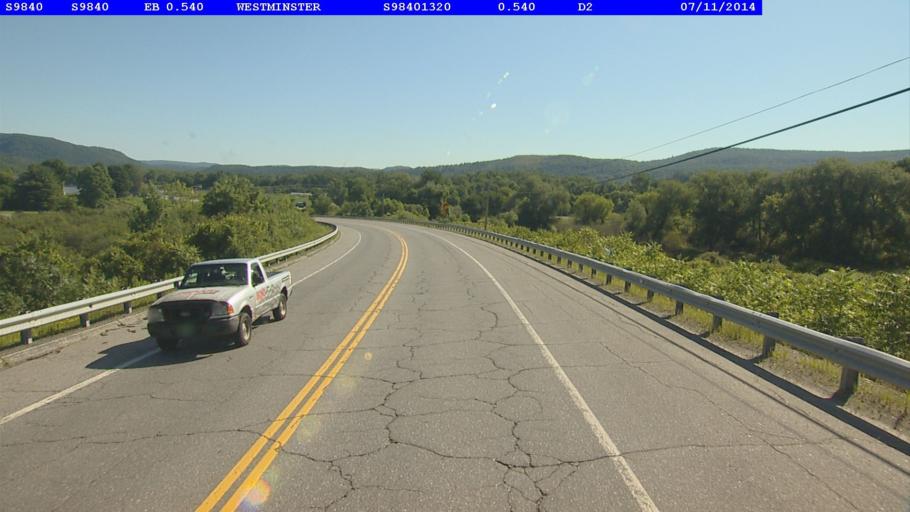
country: US
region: Vermont
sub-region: Windham County
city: Bellows Falls
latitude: 43.0920
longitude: -72.4465
